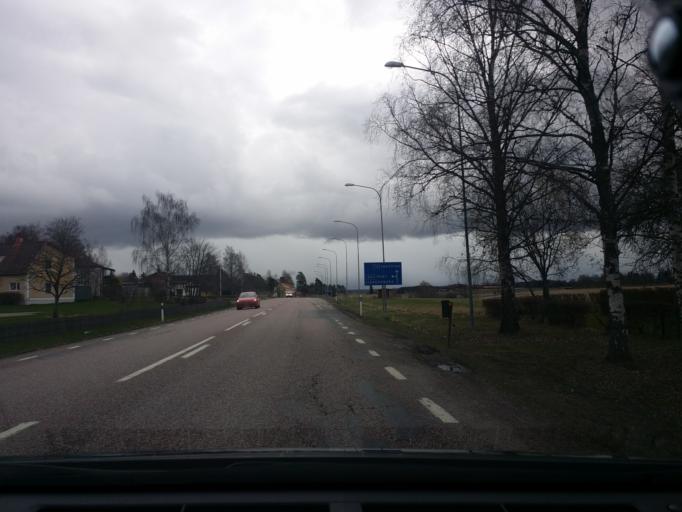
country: SE
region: Uppsala
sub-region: Enkopings Kommun
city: Irsta
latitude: 59.7732
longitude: 16.9029
